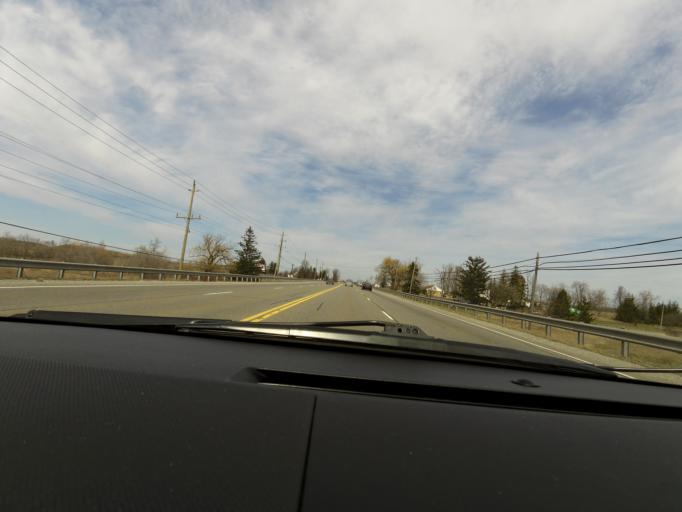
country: CA
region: Ontario
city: Ancaster
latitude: 43.1725
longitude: -79.9069
